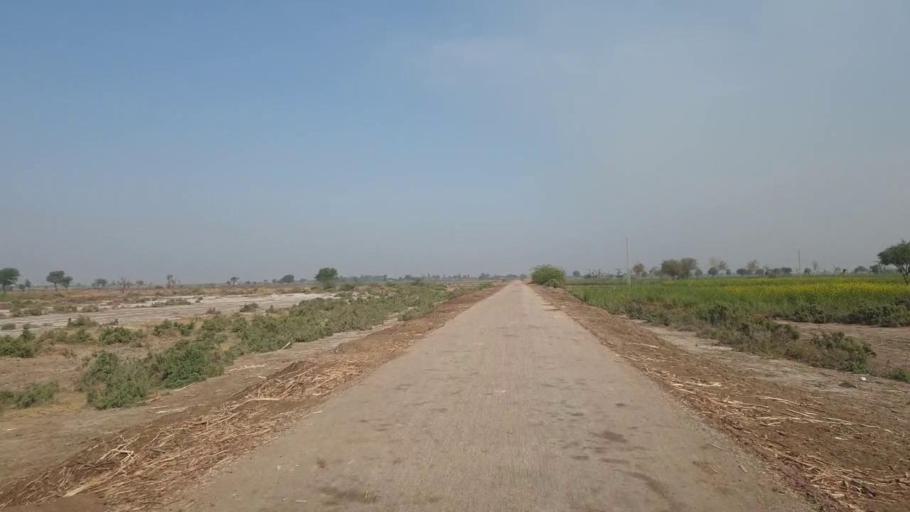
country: PK
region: Sindh
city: Mirwah Gorchani
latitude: 25.3672
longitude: 69.1615
